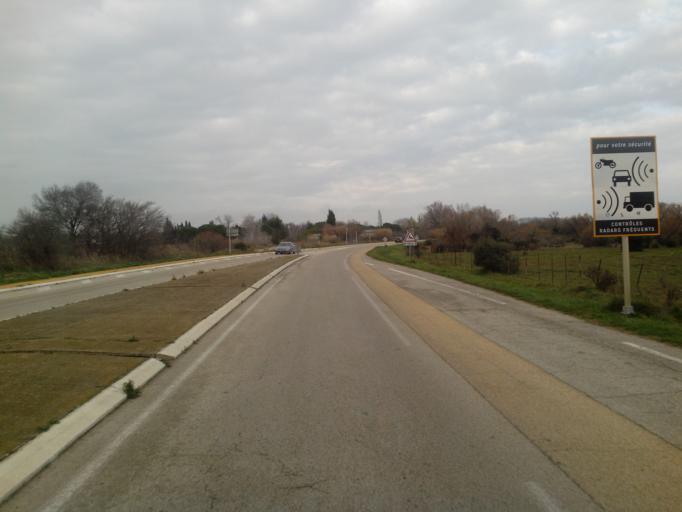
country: FR
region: Provence-Alpes-Cote d'Azur
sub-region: Departement des Bouches-du-Rhone
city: Saintes-Maries-de-la-Mer
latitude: 43.5470
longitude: 4.4013
